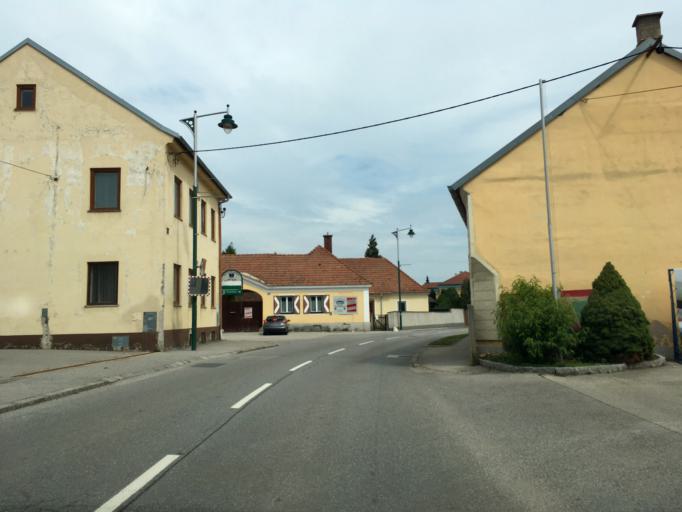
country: AT
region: Lower Austria
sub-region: Politischer Bezirk Wiener Neustadt
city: Bad Erlach
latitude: 47.7287
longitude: 16.2137
